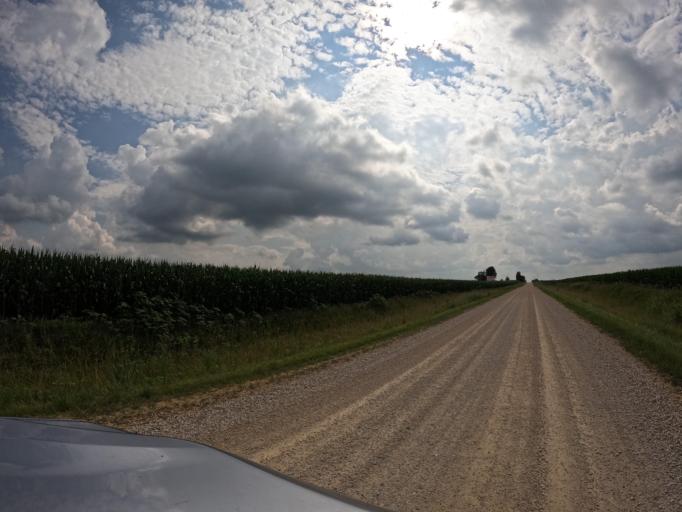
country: US
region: Iowa
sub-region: Clinton County
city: Camanche
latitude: 41.8012
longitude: -90.3750
